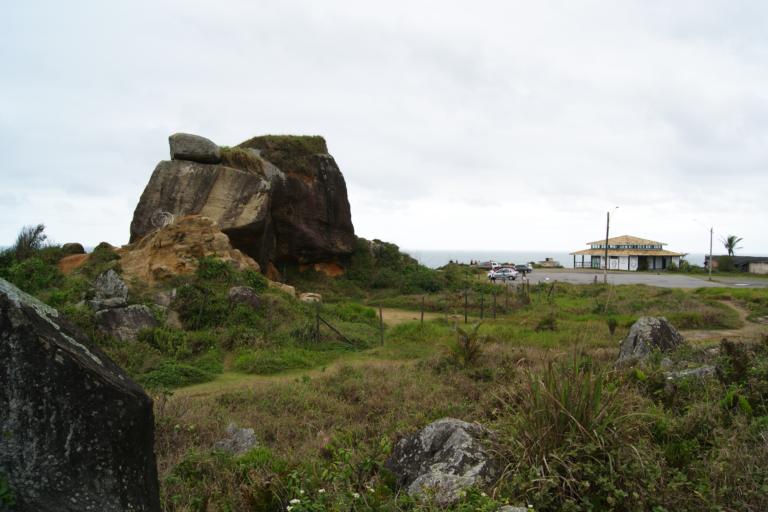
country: BR
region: Sao Paulo
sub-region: Itanhaem
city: Itanhaem
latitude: -24.1989
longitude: -46.8052
